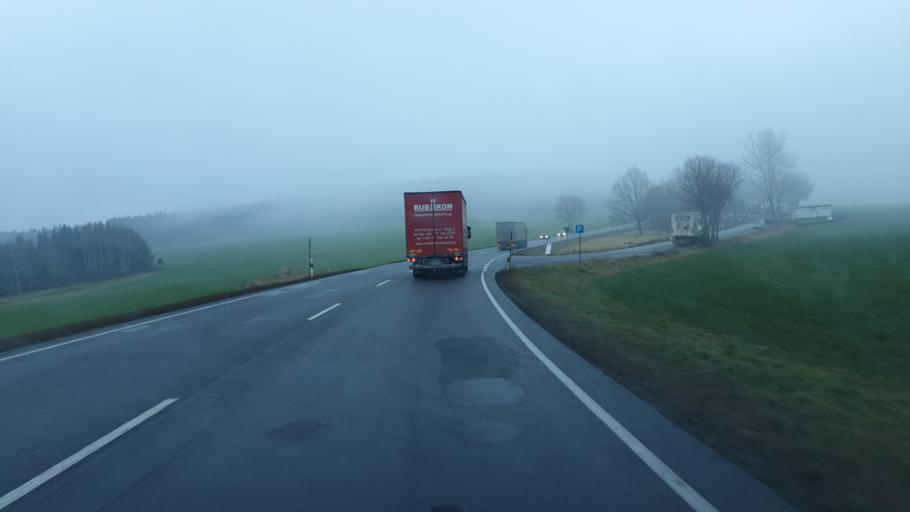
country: DE
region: Saxony
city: Grossolbersdorf
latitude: 50.7022
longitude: 13.1089
